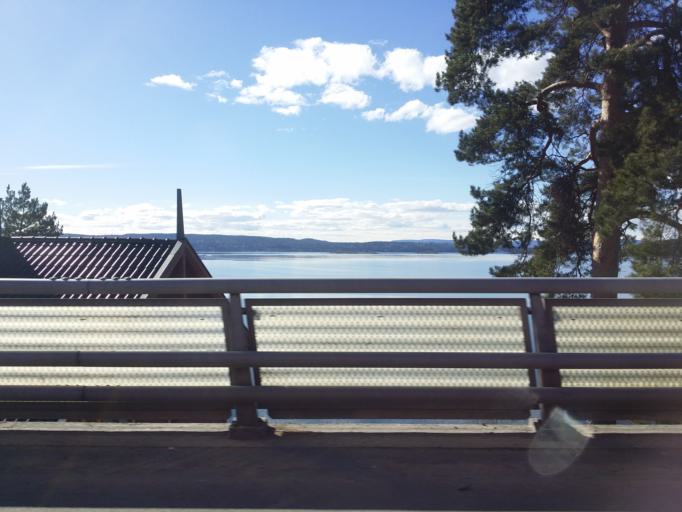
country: NO
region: Akershus
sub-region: Oppegard
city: Kolbotn
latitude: 59.8571
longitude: 10.7844
